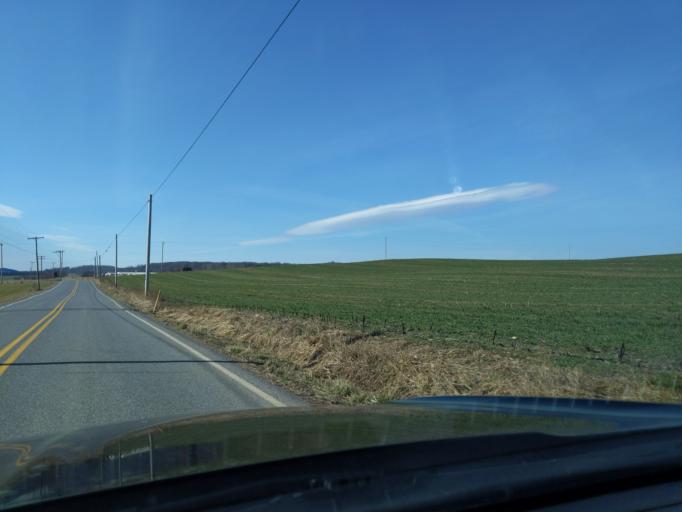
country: US
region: Pennsylvania
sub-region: Blair County
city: Martinsburg
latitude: 40.3149
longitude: -78.2780
